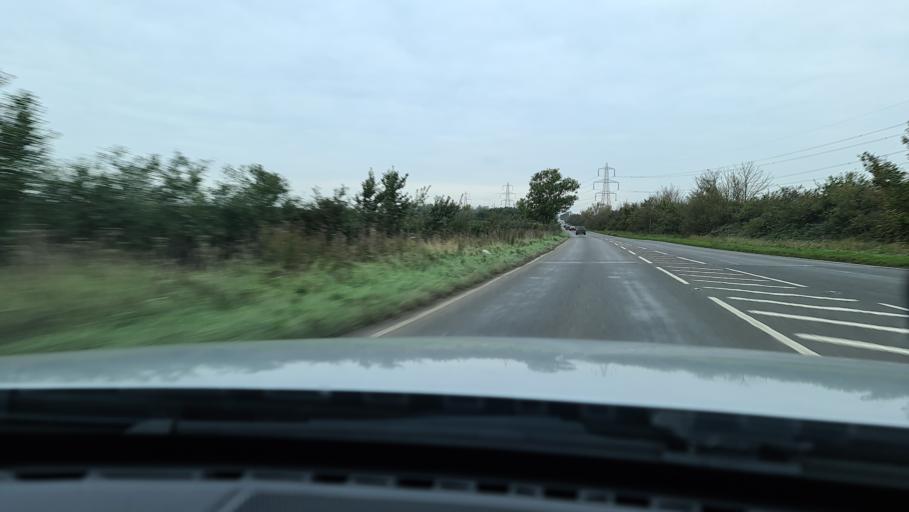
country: GB
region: England
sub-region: Buckinghamshire
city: Steeple Claydon
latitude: 51.8697
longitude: -1.0148
